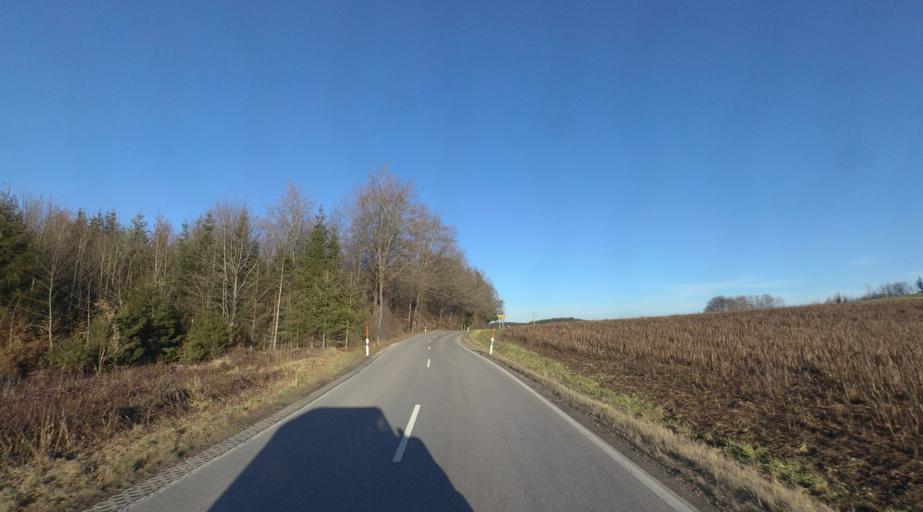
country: DE
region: Bavaria
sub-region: Upper Bavaria
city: Palling
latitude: 48.0051
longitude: 12.6831
